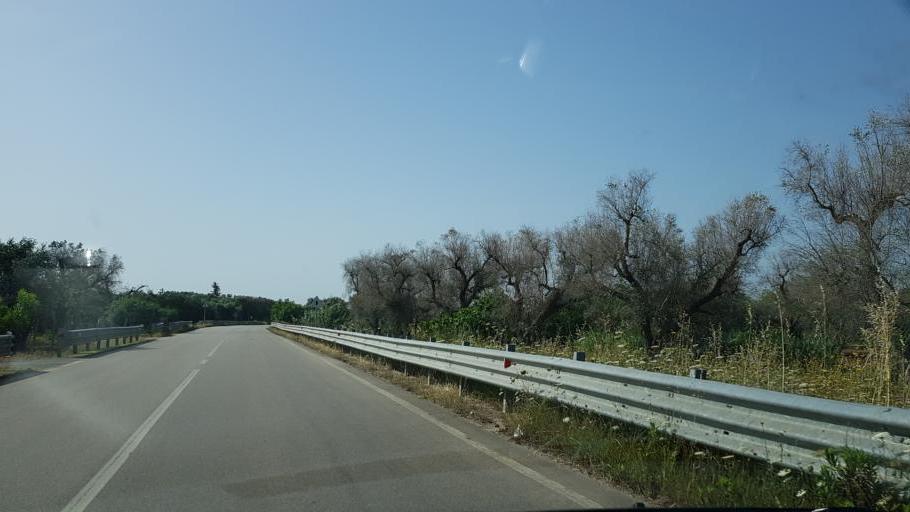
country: IT
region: Apulia
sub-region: Provincia di Brindisi
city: Mesagne
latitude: 40.4939
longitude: 17.8317
